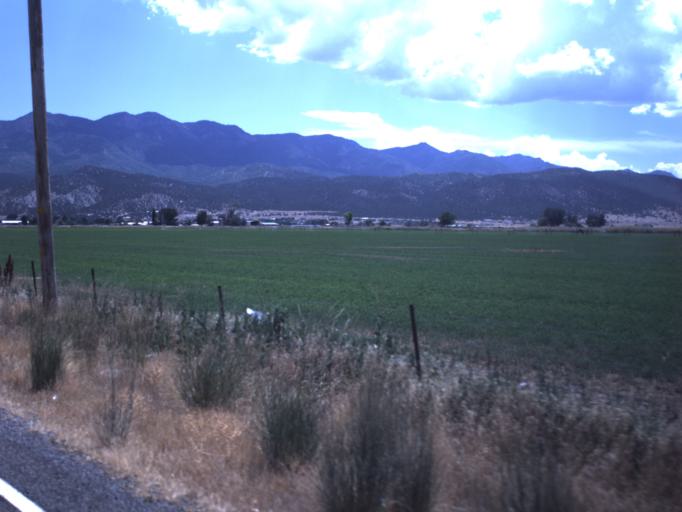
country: US
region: Utah
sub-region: Juab County
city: Nephi
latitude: 39.7100
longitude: -111.8591
